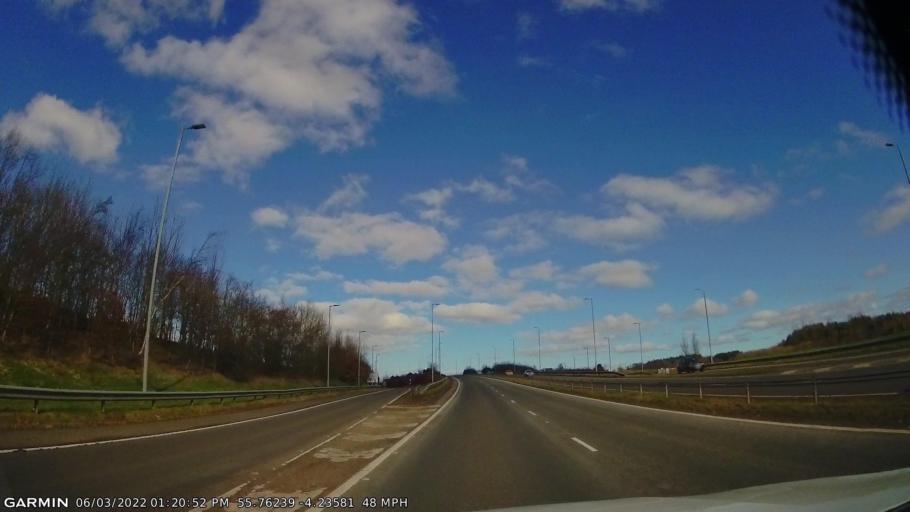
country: GB
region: Scotland
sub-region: Glasgow City
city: Carmunnock
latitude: 55.7624
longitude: -4.2358
